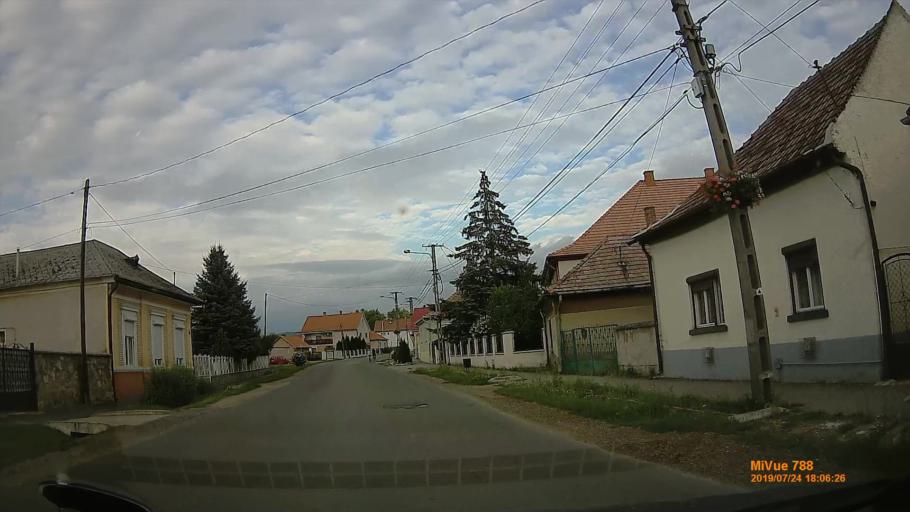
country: HU
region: Borsod-Abauj-Zemplen
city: Abaujszanto
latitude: 48.2837
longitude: 21.1831
